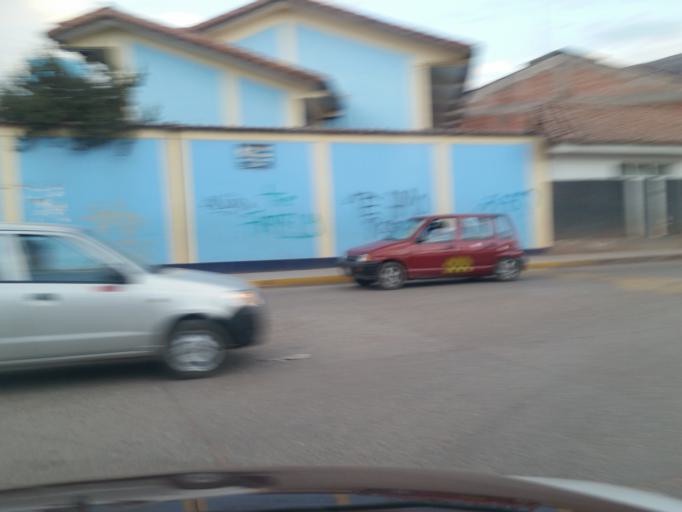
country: PE
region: Cusco
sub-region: Provincia de Cusco
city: Cusco
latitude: -13.5307
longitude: -71.9601
